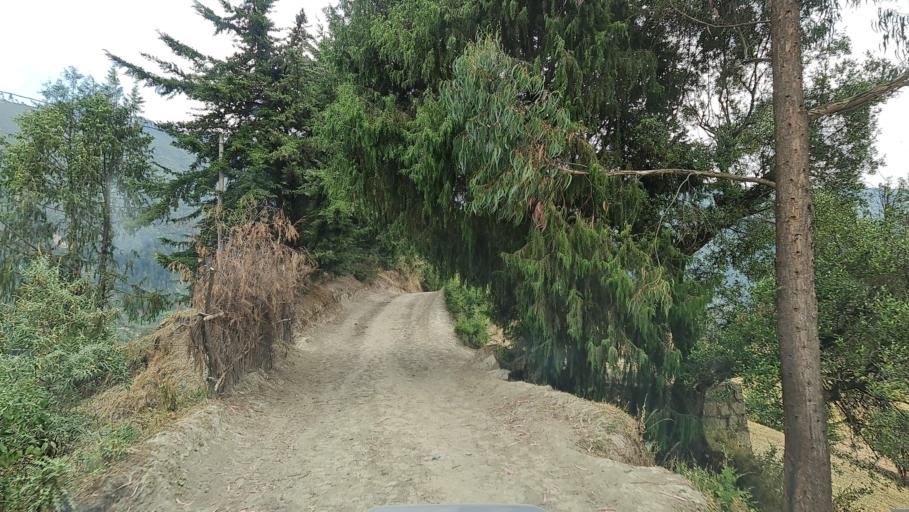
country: ET
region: Oromiya
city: Hagere Hiywet
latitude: 8.7993
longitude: 37.8913
